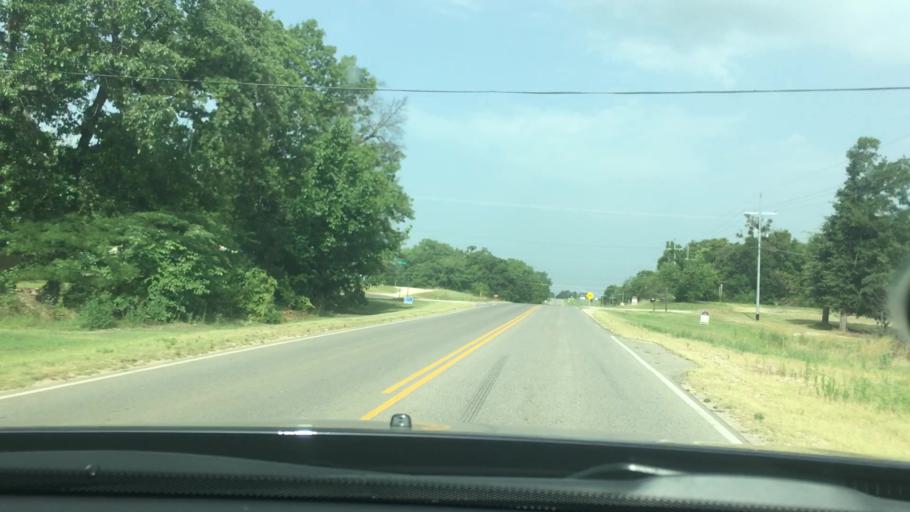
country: US
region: Oklahoma
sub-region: Pontotoc County
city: Ada
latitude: 34.7821
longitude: -96.7715
